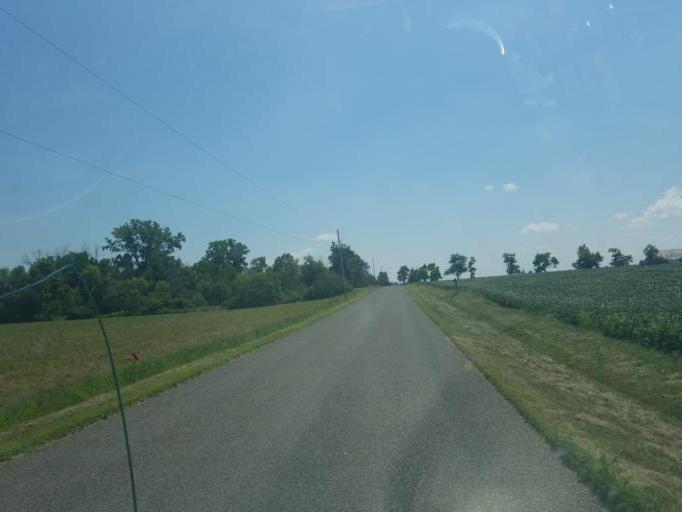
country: US
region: Ohio
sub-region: Auglaize County
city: Wapakoneta
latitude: 40.5320
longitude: -84.2311
